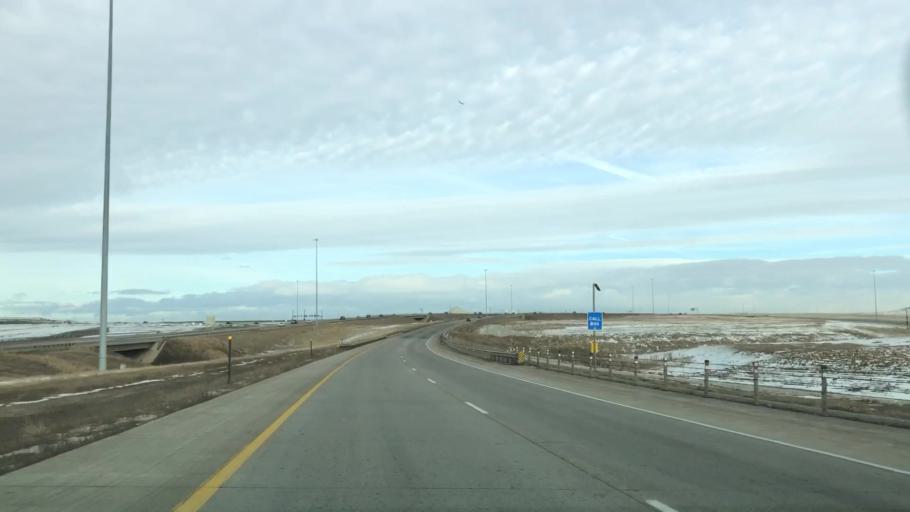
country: US
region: Colorado
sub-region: Adams County
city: Aurora
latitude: 39.8313
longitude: -104.7778
